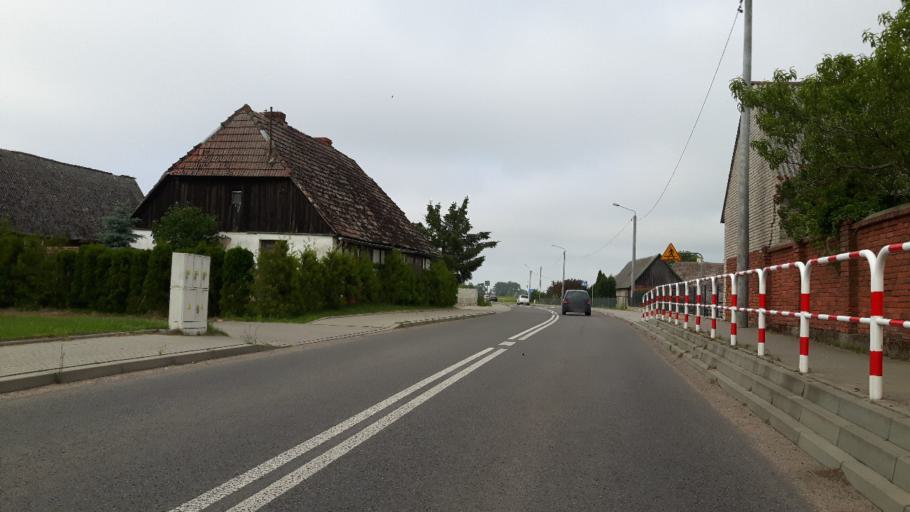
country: PL
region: West Pomeranian Voivodeship
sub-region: Powiat koszalinski
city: Sianow
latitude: 54.3334
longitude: 16.3142
